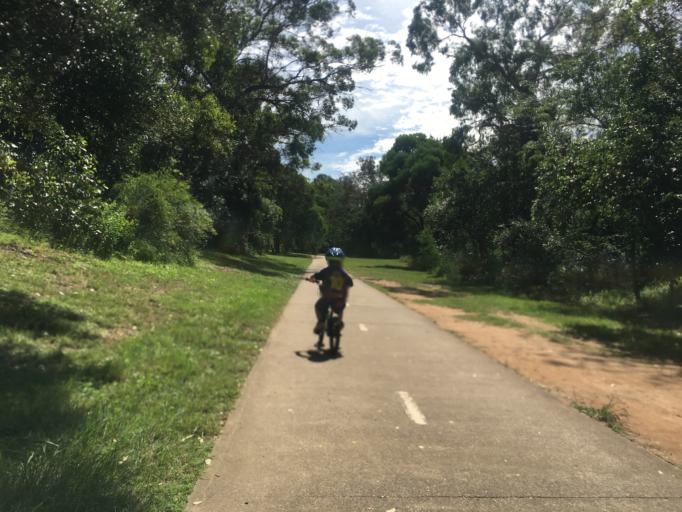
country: AU
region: New South Wales
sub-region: Camden
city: Camden South
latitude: -34.0748
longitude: 150.7006
